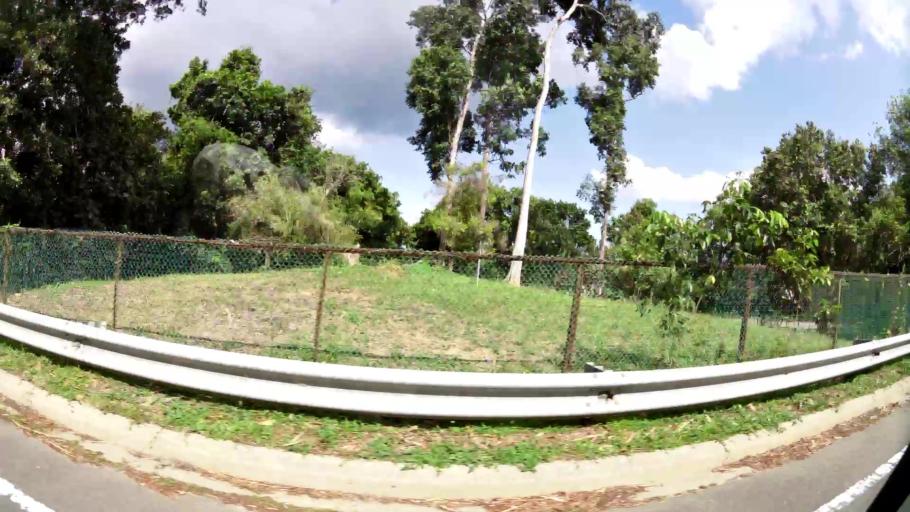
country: BN
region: Brunei and Muara
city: Bandar Seri Begawan
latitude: 4.9599
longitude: 114.9512
